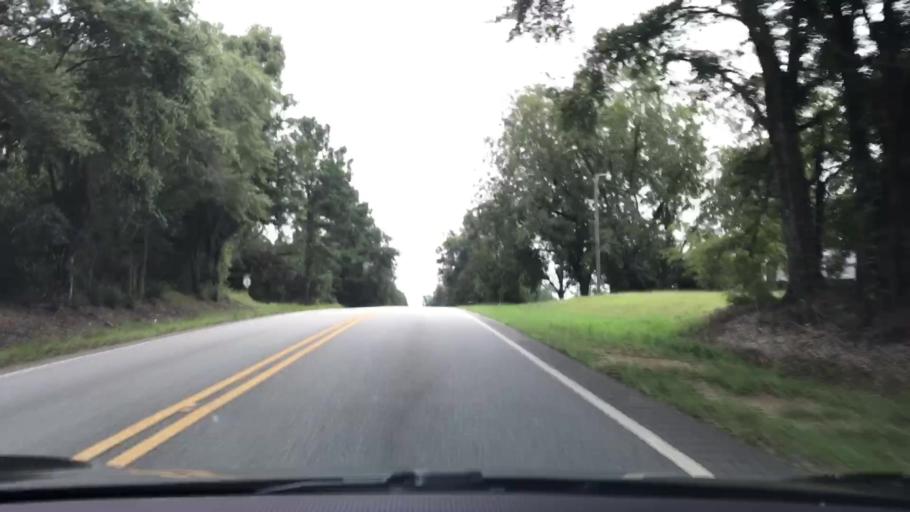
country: US
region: Alabama
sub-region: Geneva County
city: Samson
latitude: 31.0291
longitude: -86.1121
